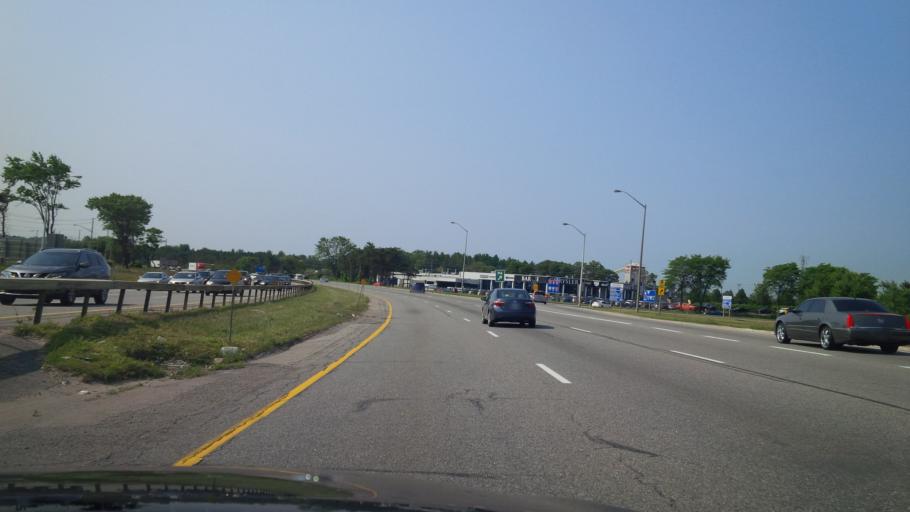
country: CA
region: Ontario
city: Barrie
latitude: 44.3792
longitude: -79.7115
